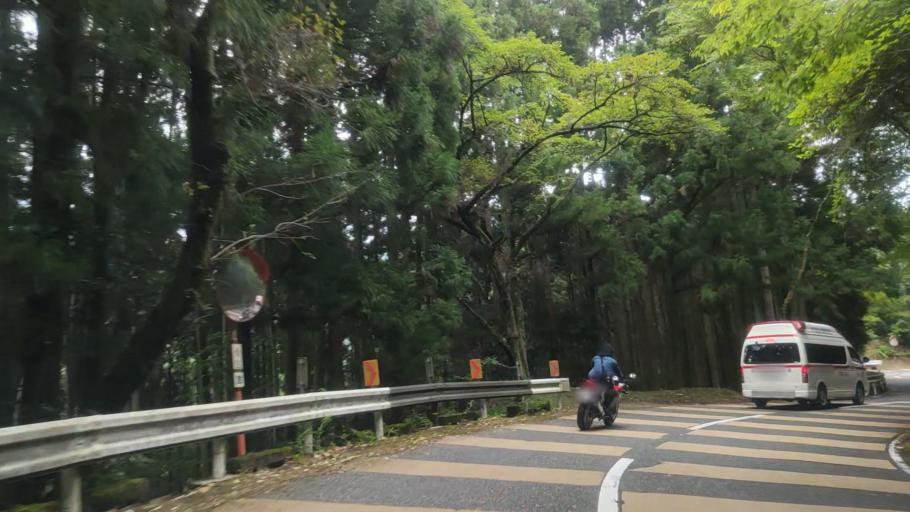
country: JP
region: Wakayama
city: Koya
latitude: 34.2229
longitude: 135.5374
